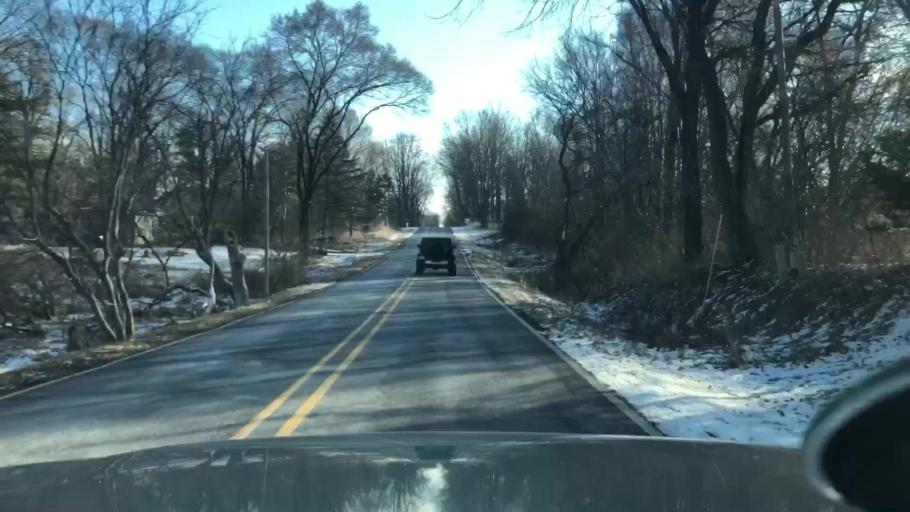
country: US
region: Michigan
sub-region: Jackson County
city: Vandercook Lake
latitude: 42.1354
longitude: -84.4517
